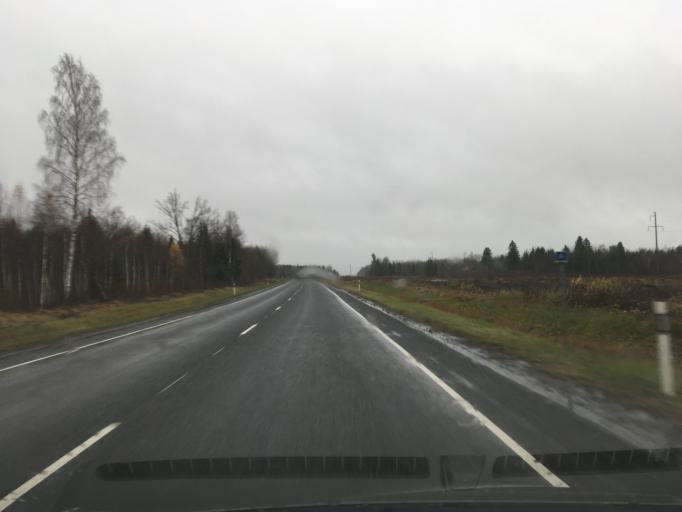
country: EE
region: Harju
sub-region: Nissi vald
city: Turba
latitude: 58.9429
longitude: 24.0869
